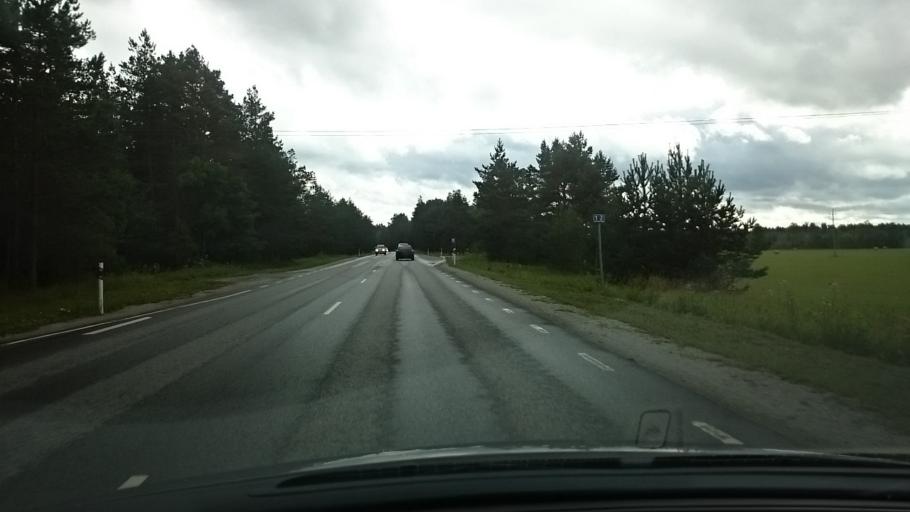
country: EE
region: Harju
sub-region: Keila linn
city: Keila
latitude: 59.2536
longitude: 24.2840
